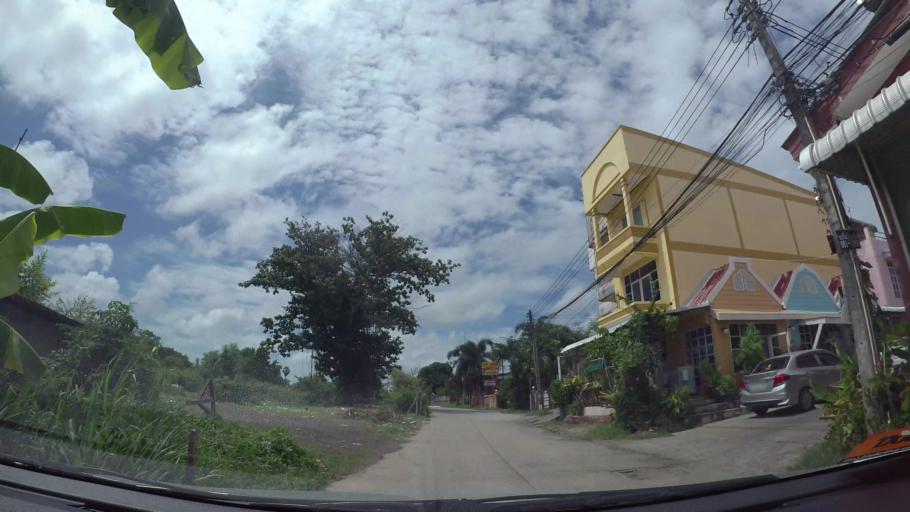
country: TH
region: Chon Buri
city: Sattahip
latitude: 12.6748
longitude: 100.8996
